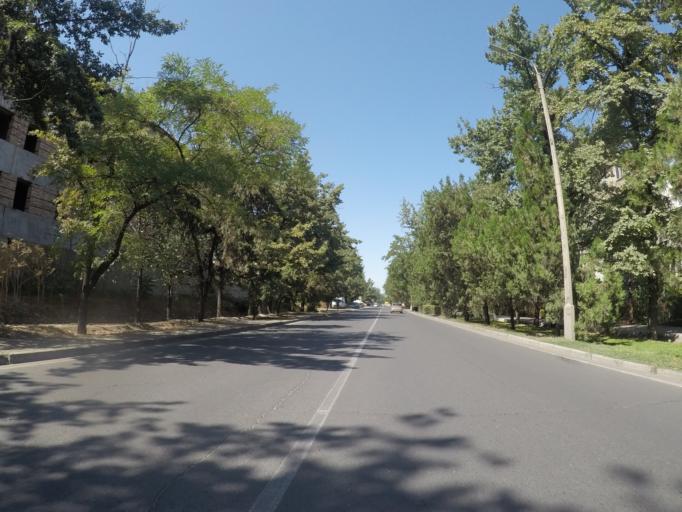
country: KG
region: Chuy
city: Bishkek
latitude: 42.8813
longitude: 74.5947
